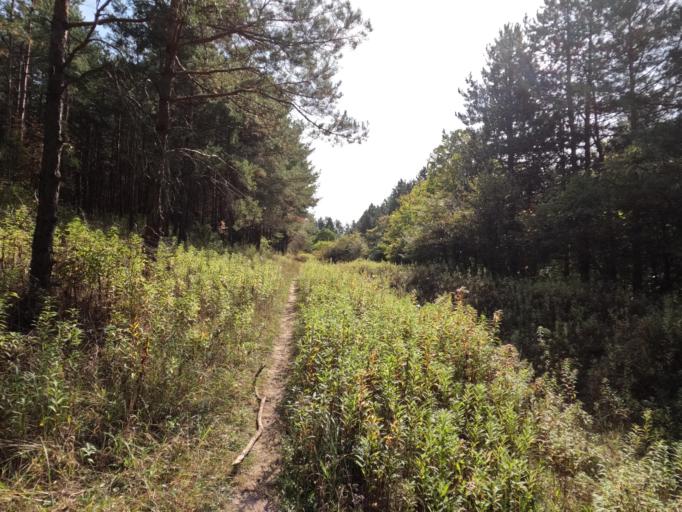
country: HU
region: Tolna
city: Szentgalpuszta
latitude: 46.3489
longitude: 18.6245
